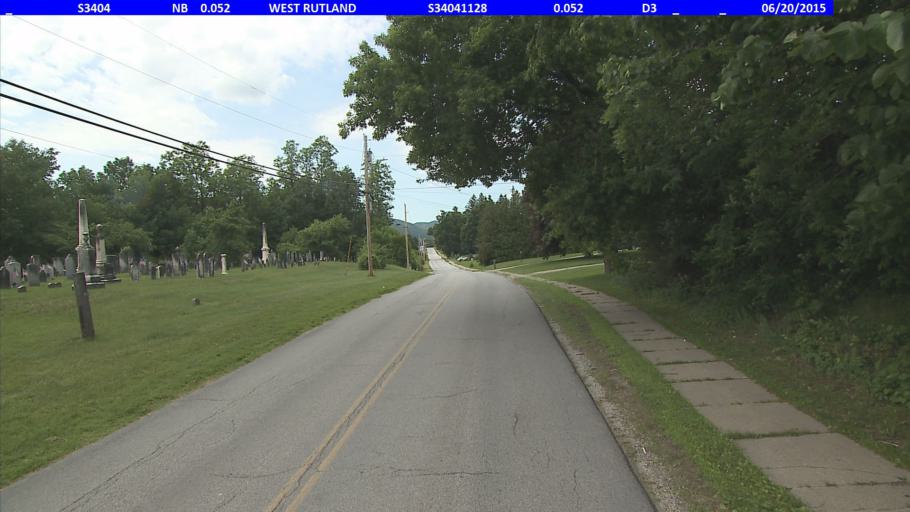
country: US
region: Vermont
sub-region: Rutland County
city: West Rutland
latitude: 43.5947
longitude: -73.0384
